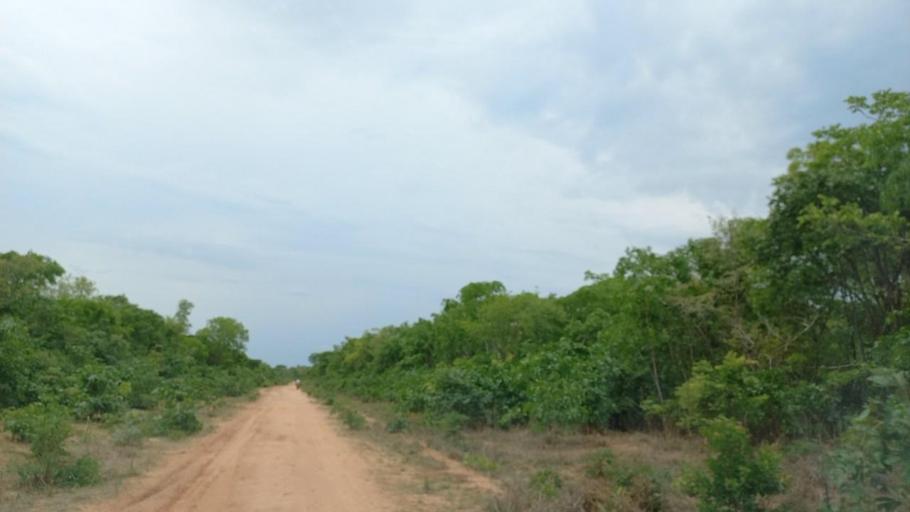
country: ZM
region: North-Western
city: Mufumbwe
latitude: -13.6498
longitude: 24.9790
